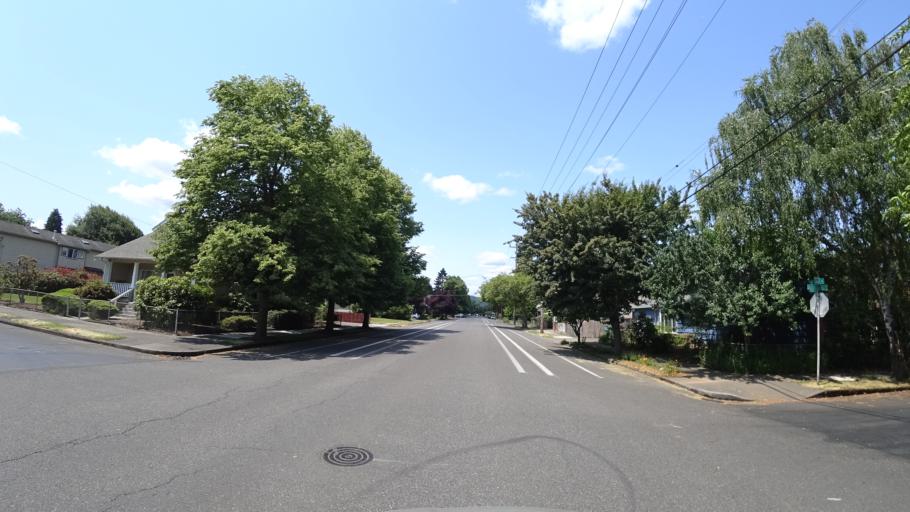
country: US
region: Oregon
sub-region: Washington County
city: West Haven
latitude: 45.5930
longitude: -122.7454
